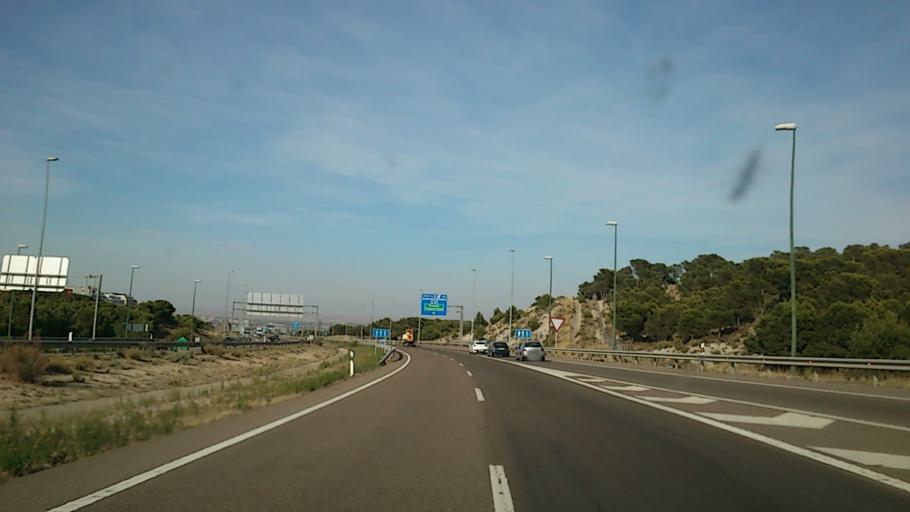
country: ES
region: Aragon
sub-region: Provincia de Zaragoza
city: Zaragoza
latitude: 41.6089
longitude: -0.8760
